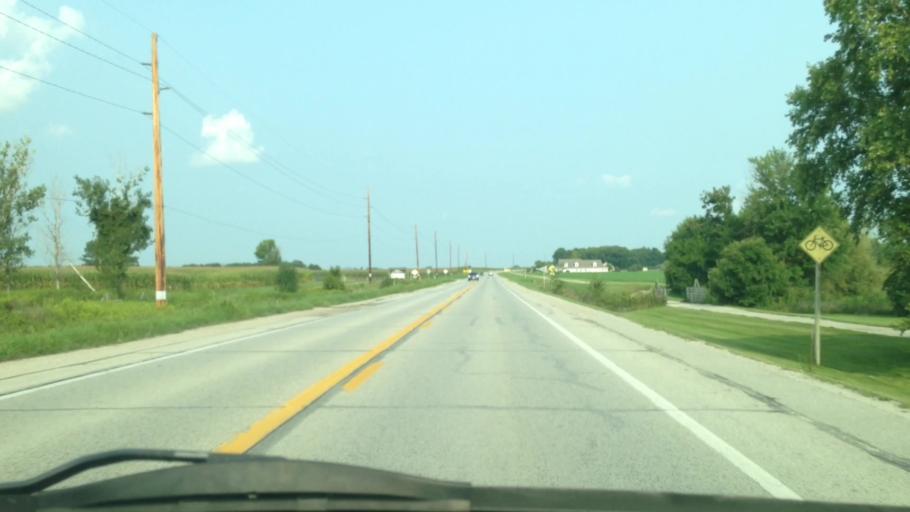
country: US
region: Iowa
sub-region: Benton County
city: Walford
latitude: 41.8035
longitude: -91.8873
